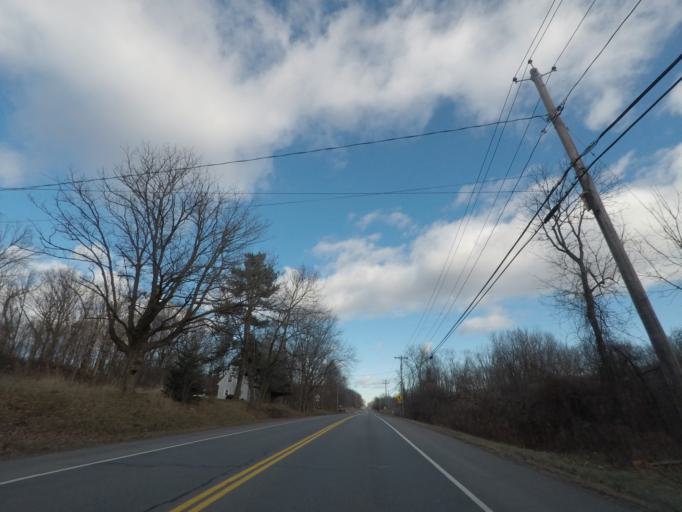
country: US
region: New York
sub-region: Saratoga County
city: Waterford
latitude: 42.7637
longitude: -73.6622
